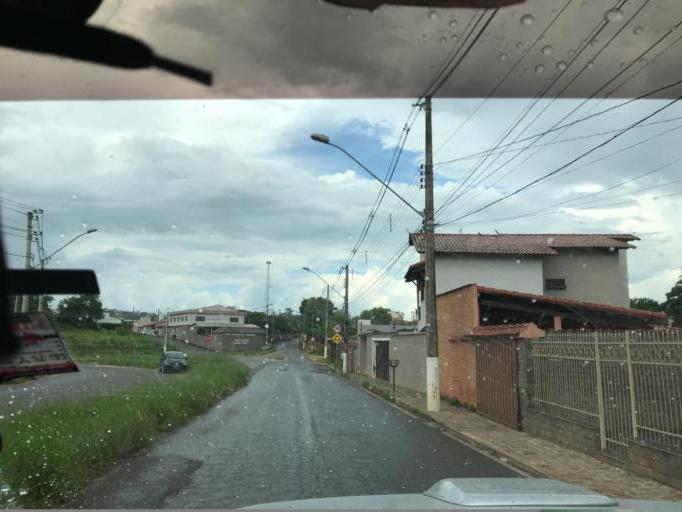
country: BR
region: Minas Gerais
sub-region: Tres Coracoes
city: Tres Coracoes
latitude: -21.7077
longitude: -45.2536
